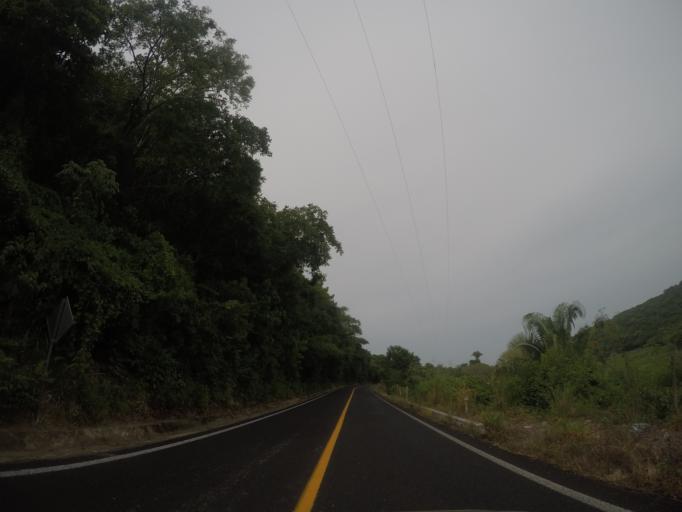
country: MX
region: Oaxaca
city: San Pedro Mixtepec
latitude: 15.9467
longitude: -97.2965
